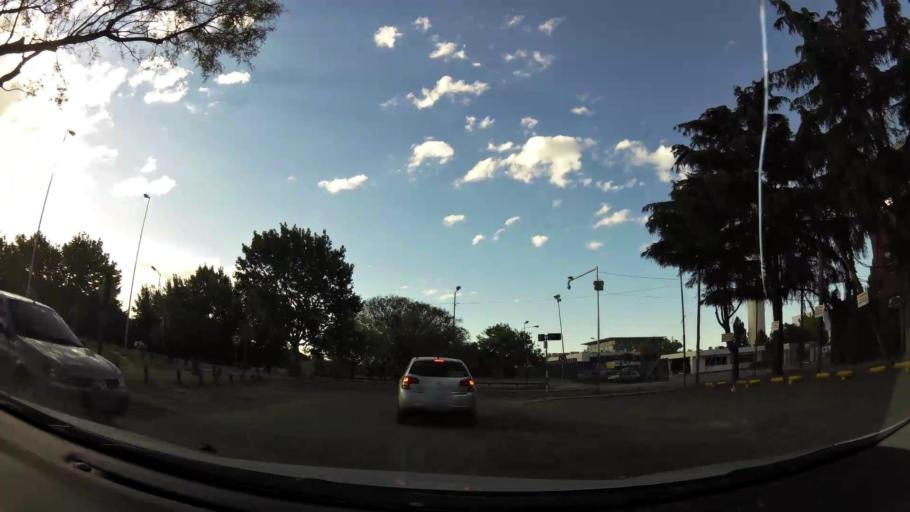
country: AR
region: Buenos Aires
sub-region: Partido de Tigre
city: Tigre
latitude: -34.4709
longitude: -58.5650
